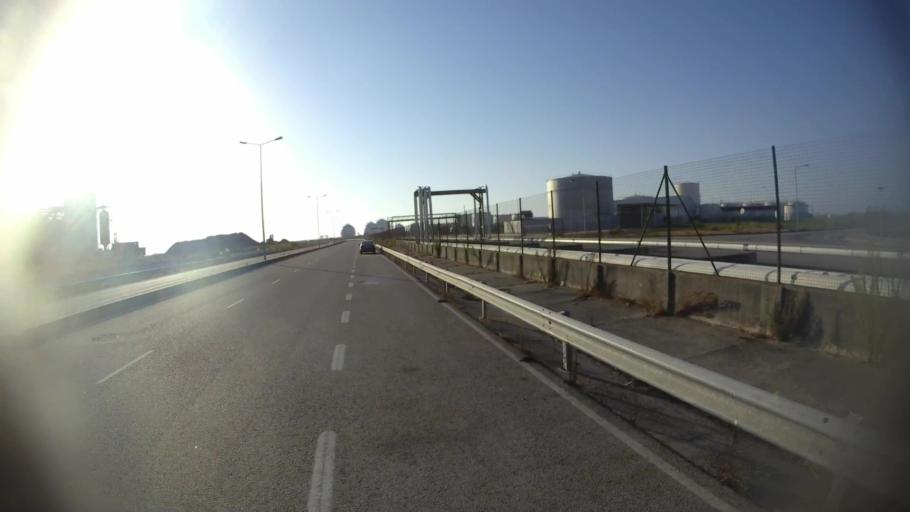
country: PT
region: Aveiro
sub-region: Ilhavo
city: Gafanha da Nazare
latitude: 40.6532
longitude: -8.7085
